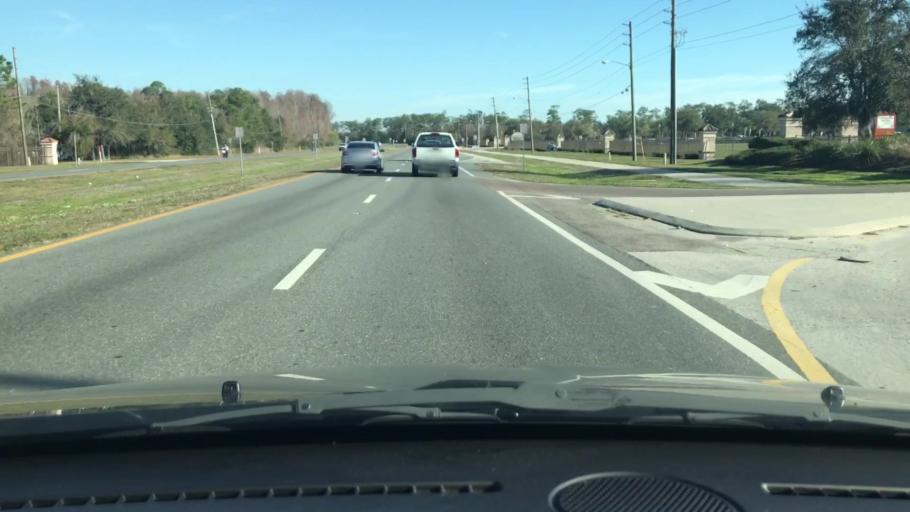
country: US
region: Florida
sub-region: Osceola County
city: Poinciana
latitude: 28.1846
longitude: -81.4393
